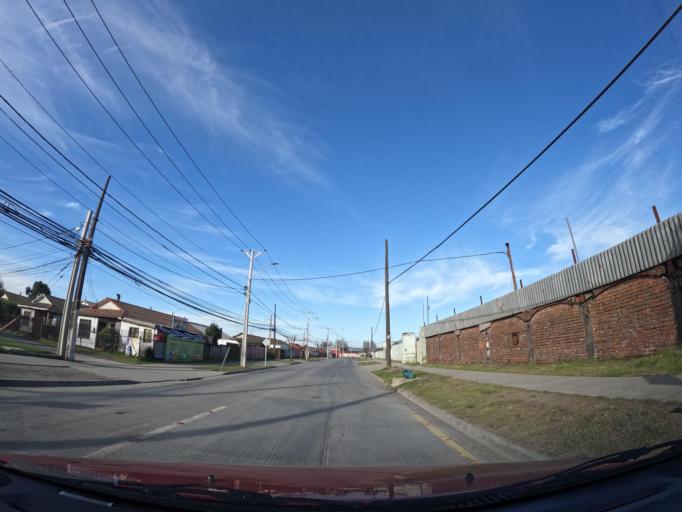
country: CL
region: Biobio
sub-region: Provincia de Concepcion
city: Talcahuano
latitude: -36.7596
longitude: -73.0827
